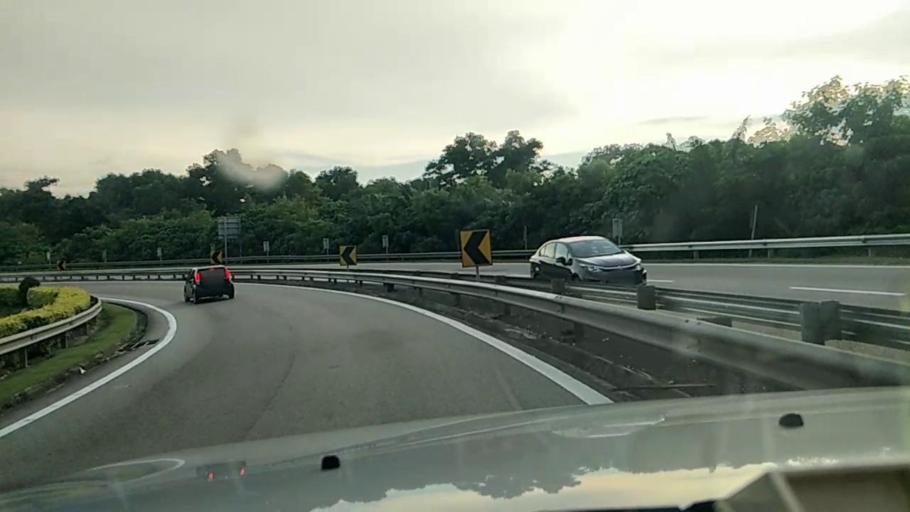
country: MY
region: Selangor
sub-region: Petaling
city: Petaling Jaya
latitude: 3.1071
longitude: 101.5889
